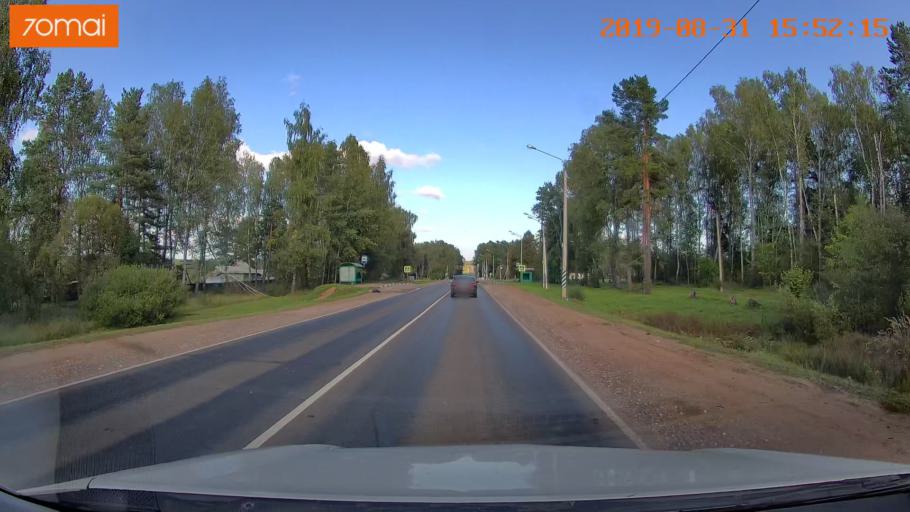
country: RU
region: Kaluga
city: Yukhnov
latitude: 54.7073
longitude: 35.1108
